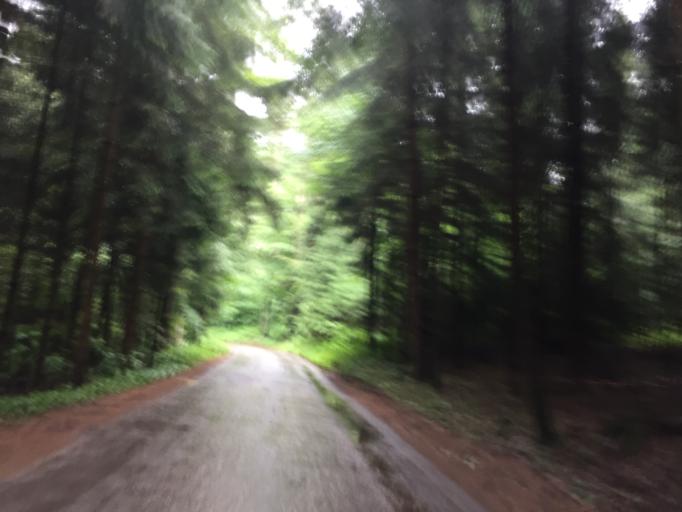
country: CH
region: Bern
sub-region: Bern-Mittelland District
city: Biglen
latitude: 46.9113
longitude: 7.5958
